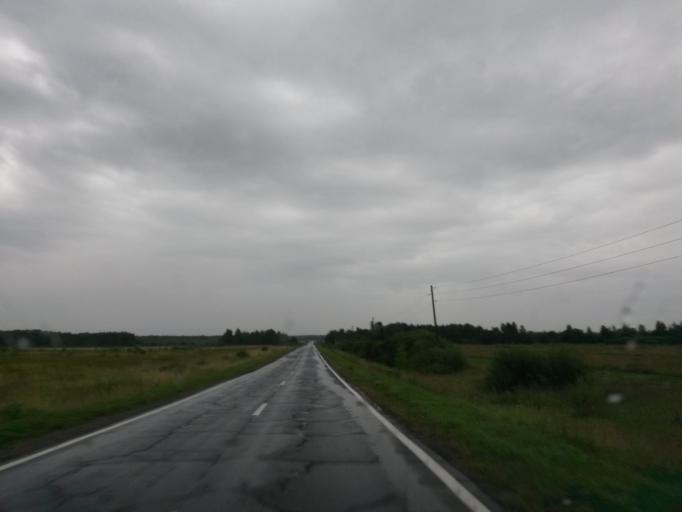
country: RU
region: Jaroslavl
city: Tutayev
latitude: 57.9496
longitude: 39.4503
